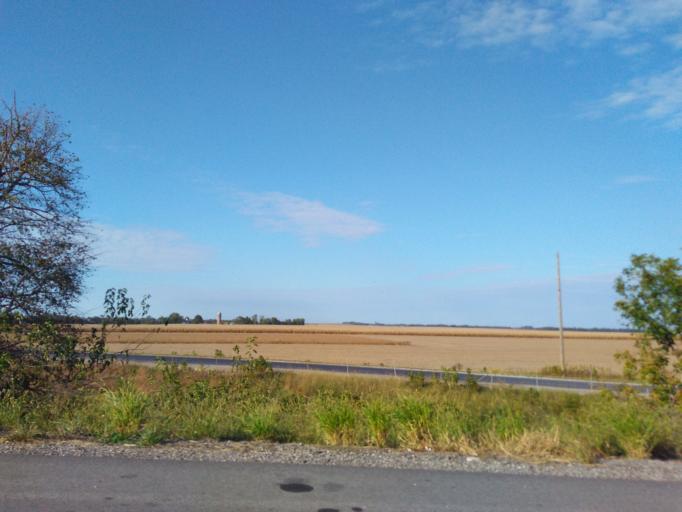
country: US
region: Illinois
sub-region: Madison County
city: Highland
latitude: 38.7877
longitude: -89.6303
